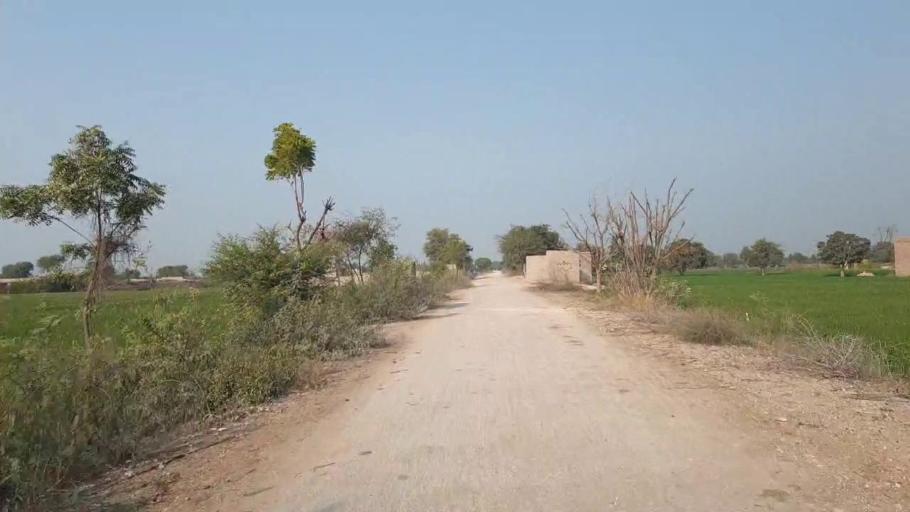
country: PK
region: Sindh
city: Hala
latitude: 25.8668
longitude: 68.4618
